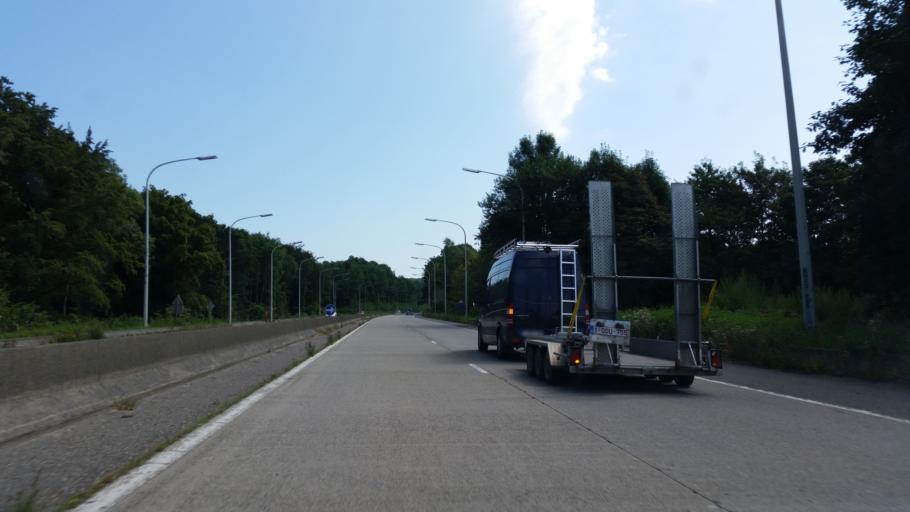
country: BE
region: Wallonia
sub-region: Province de Namur
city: Hamois
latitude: 50.3097
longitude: 5.1499
